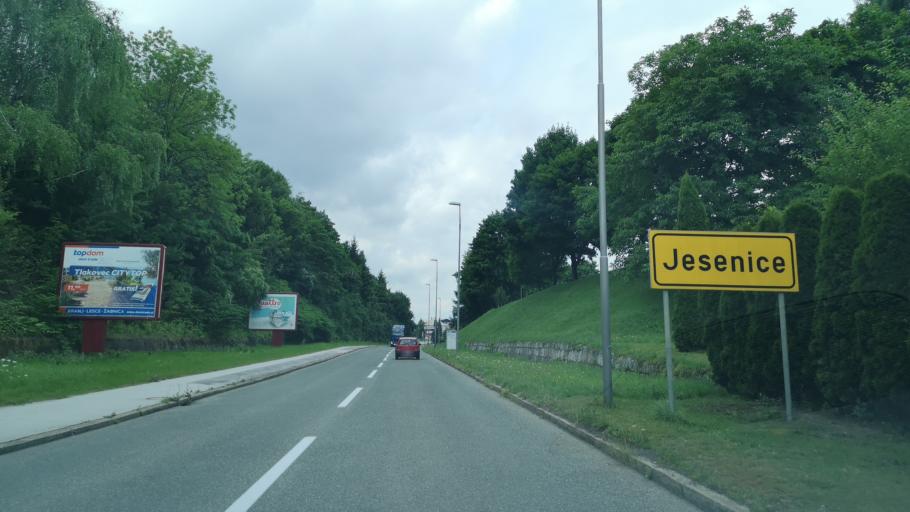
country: SI
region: Jesenice
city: Jesenice
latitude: 46.4293
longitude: 14.0767
